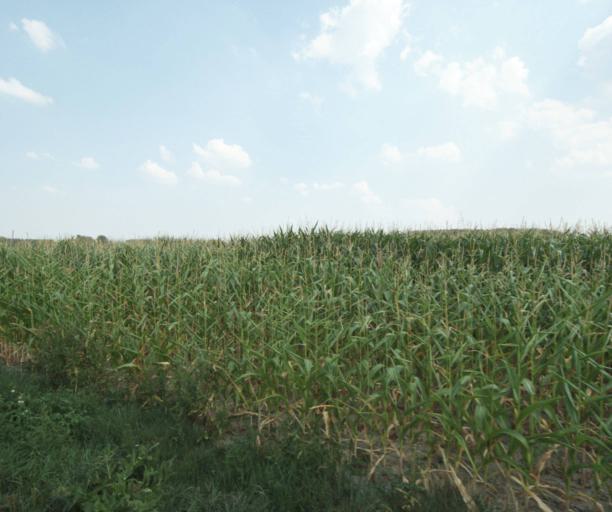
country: FR
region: Nord-Pas-de-Calais
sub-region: Departement du Nord
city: Quesnoy-sur-Deule
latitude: 50.7312
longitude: 3.0016
